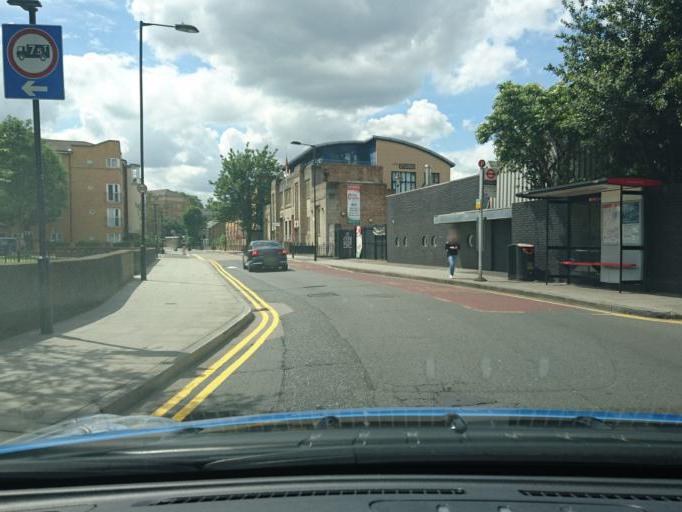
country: GB
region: England
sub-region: Greater London
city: Hackney
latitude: 51.5475
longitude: -0.0285
